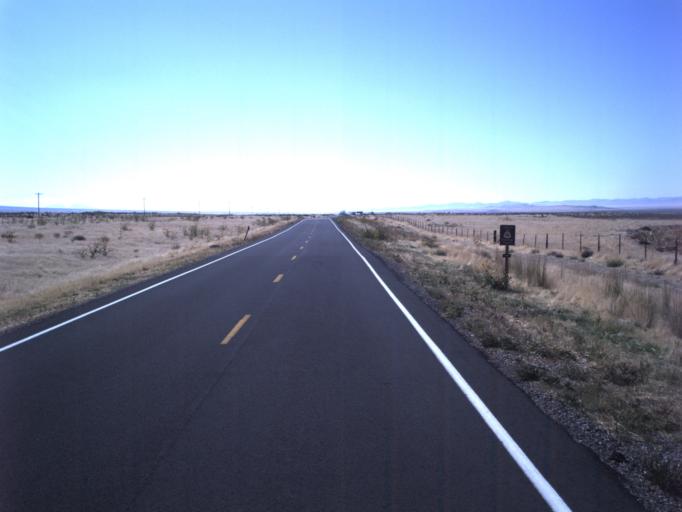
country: US
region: Utah
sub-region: Tooele County
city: Grantsville
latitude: 40.5179
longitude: -112.7477
